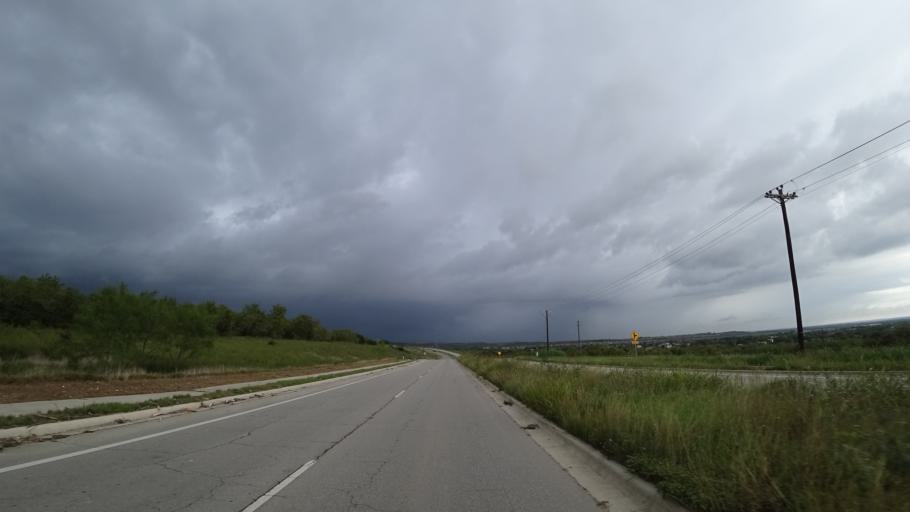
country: US
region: Texas
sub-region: Travis County
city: Onion Creek
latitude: 30.1576
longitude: -97.7293
